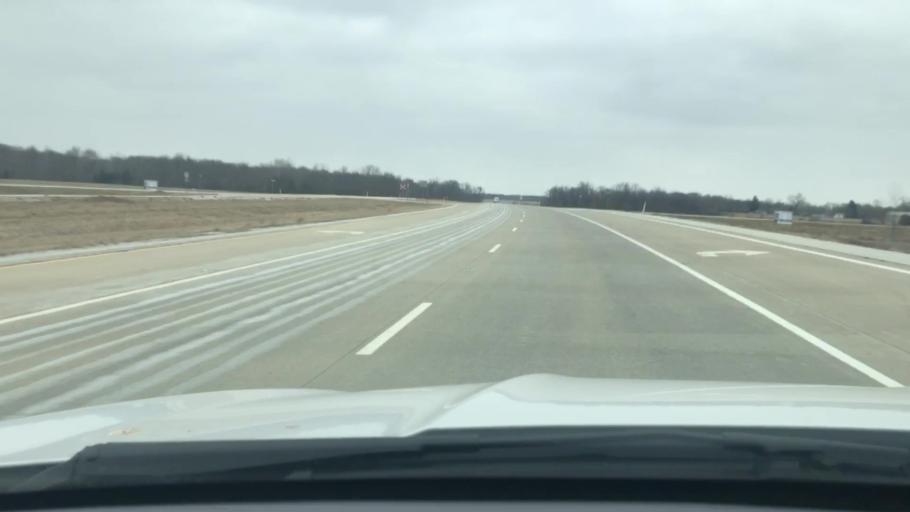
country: US
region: Indiana
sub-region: Tippecanoe County
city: Battle Ground
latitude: 40.4829
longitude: -86.7753
